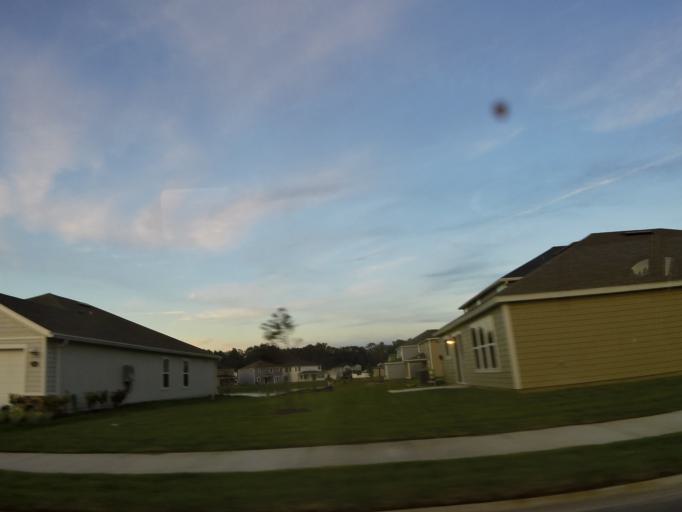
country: US
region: Florida
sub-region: Saint Johns County
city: Fruit Cove
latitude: 30.1500
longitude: -81.5191
